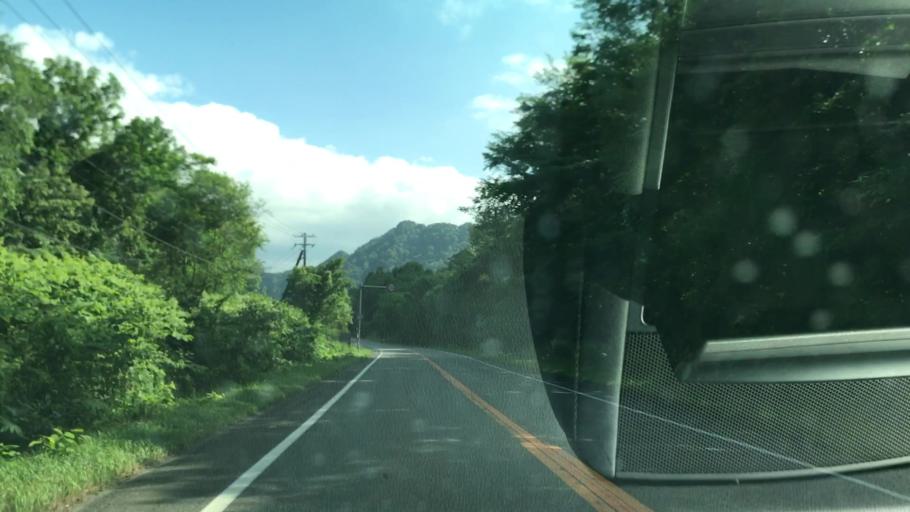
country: JP
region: Hokkaido
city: Shizunai-furukawacho
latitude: 42.8397
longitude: 142.4159
